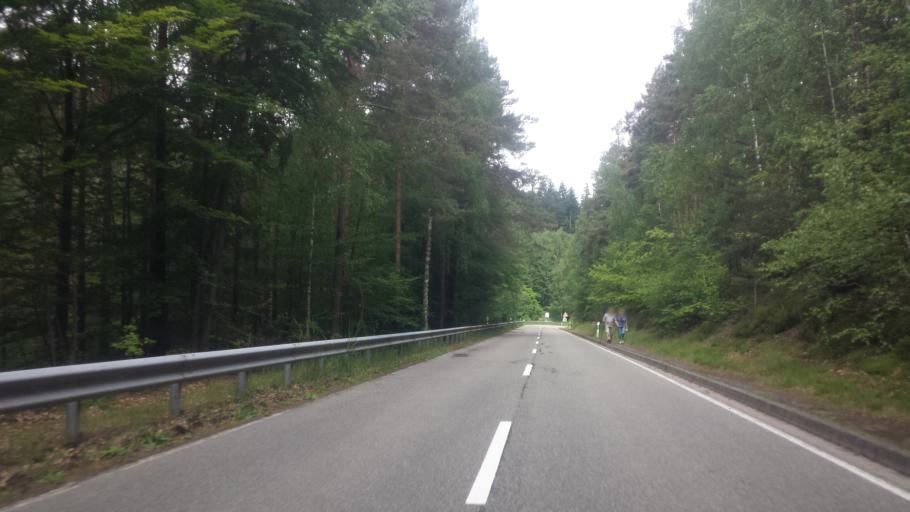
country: DE
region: Rheinland-Pfalz
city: Lindenberg
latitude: 49.3978
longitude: 8.1021
